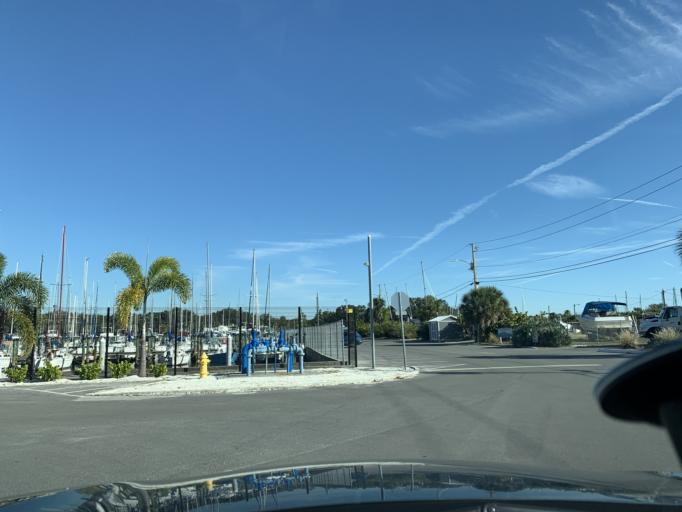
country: US
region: Florida
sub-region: Pinellas County
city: Gulfport
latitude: 27.7396
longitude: -82.6972
